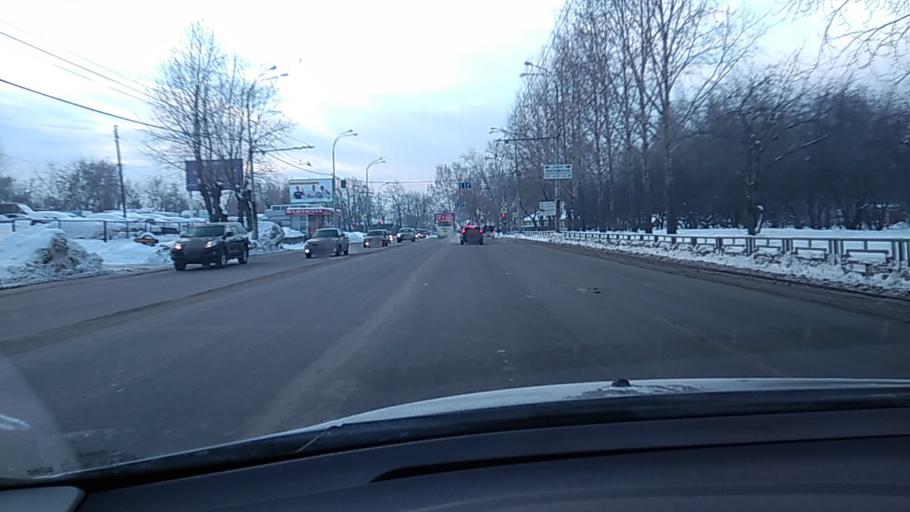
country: RU
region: Sverdlovsk
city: Yekaterinburg
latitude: 56.8070
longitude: 60.5944
